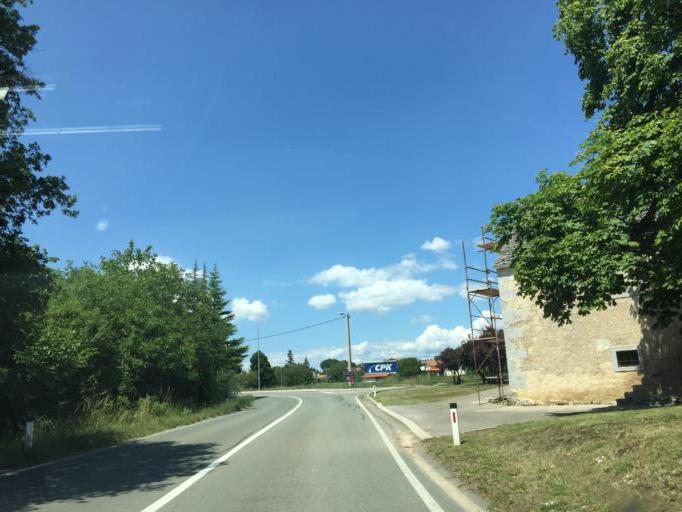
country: SI
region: Sezana
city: Sezana
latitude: 45.7411
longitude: 13.8649
